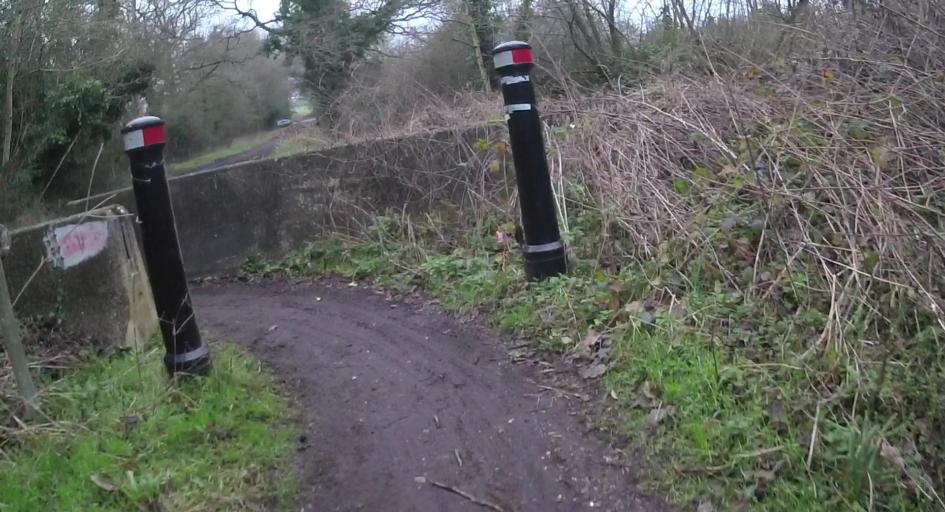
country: GB
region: England
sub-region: Wokingham
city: Barkham
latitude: 51.3927
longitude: -0.8598
